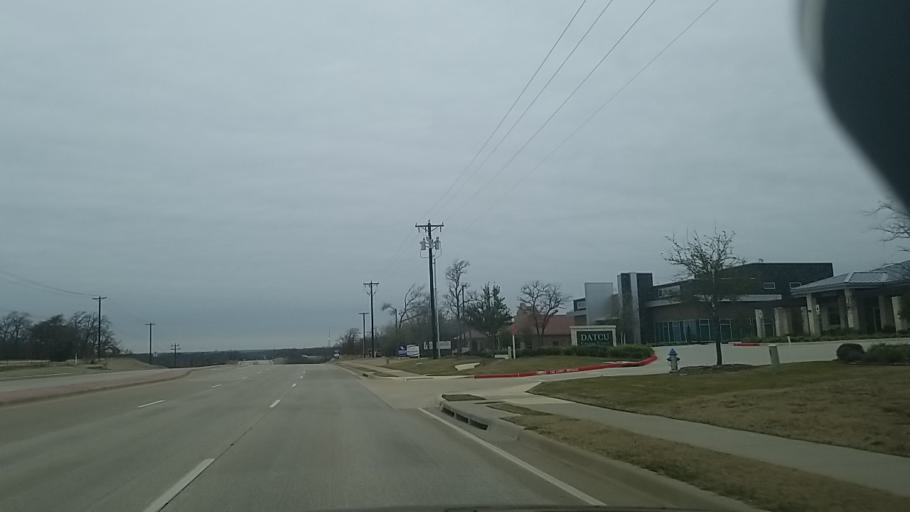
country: US
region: Texas
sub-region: Denton County
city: Hickory Creek
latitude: 33.1303
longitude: -97.0627
